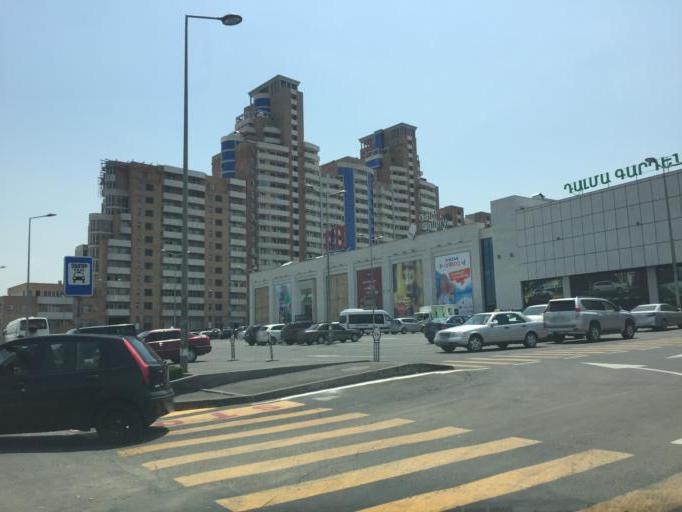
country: AM
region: Yerevan
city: Yerevan
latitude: 40.1804
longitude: 44.4885
